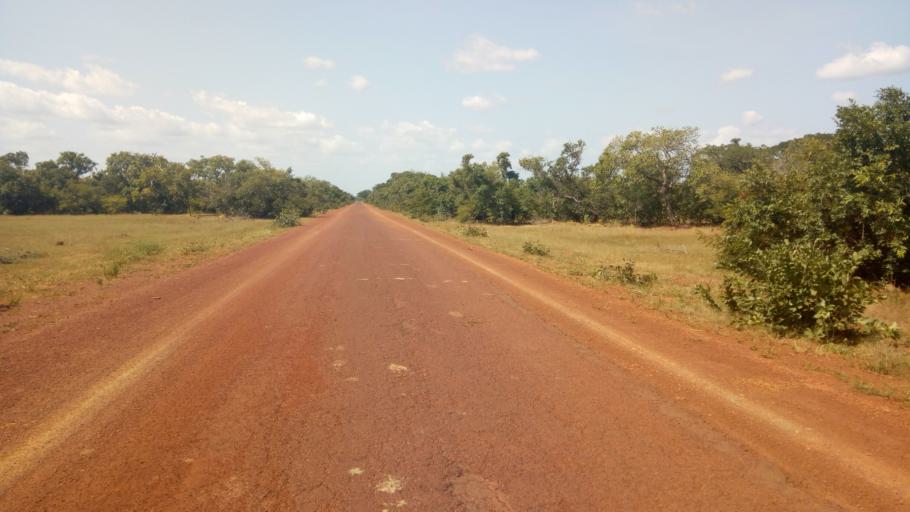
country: ML
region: Sikasso
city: Yorosso
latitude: 12.3889
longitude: -4.8824
